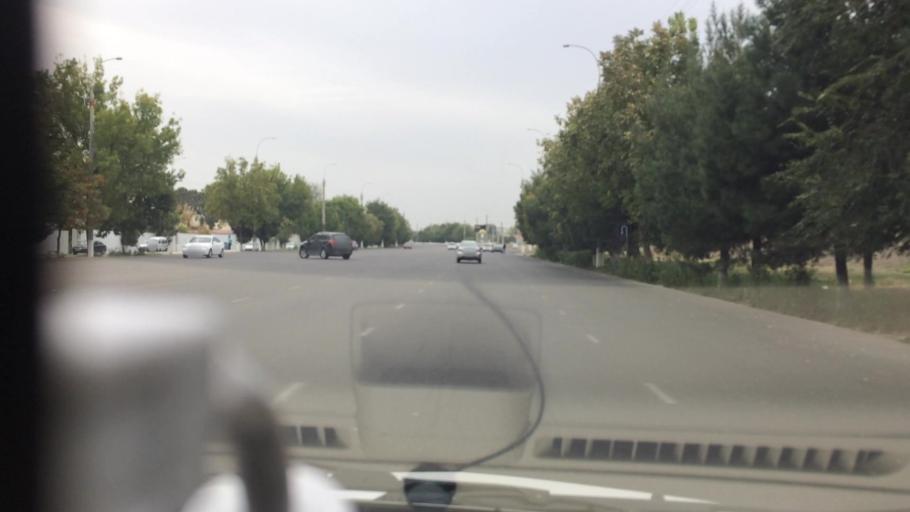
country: UZ
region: Toshkent
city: Salor
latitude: 41.3145
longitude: 69.3090
